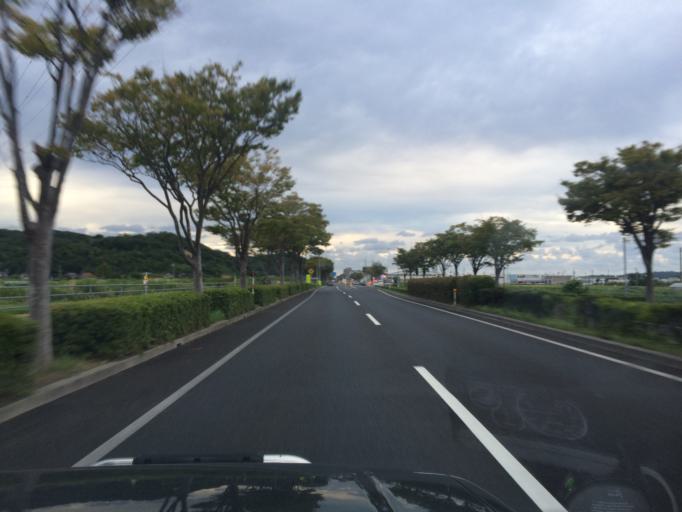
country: JP
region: Tottori
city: Tottori
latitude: 35.4853
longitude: 134.2050
